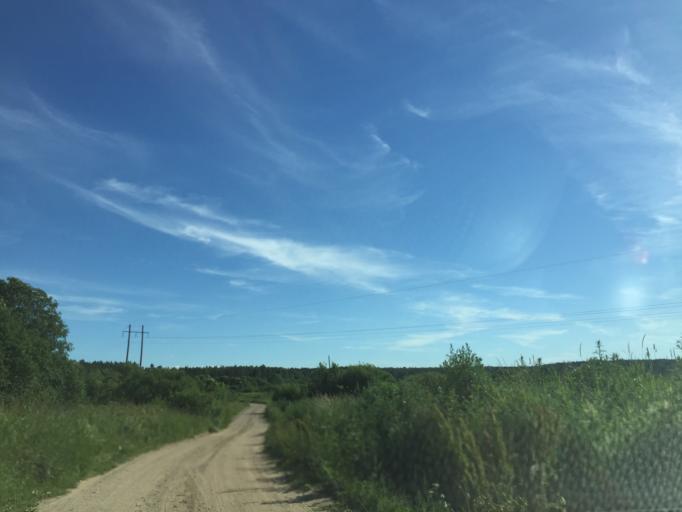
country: LV
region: Kuldigas Rajons
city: Kuldiga
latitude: 57.0735
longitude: 21.8265
